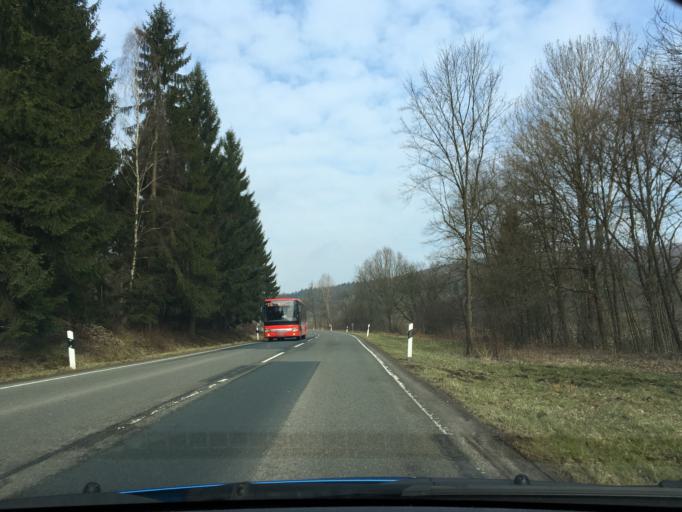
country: DE
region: Lower Saxony
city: Bodenfelde
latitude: 51.7142
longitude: 9.5312
